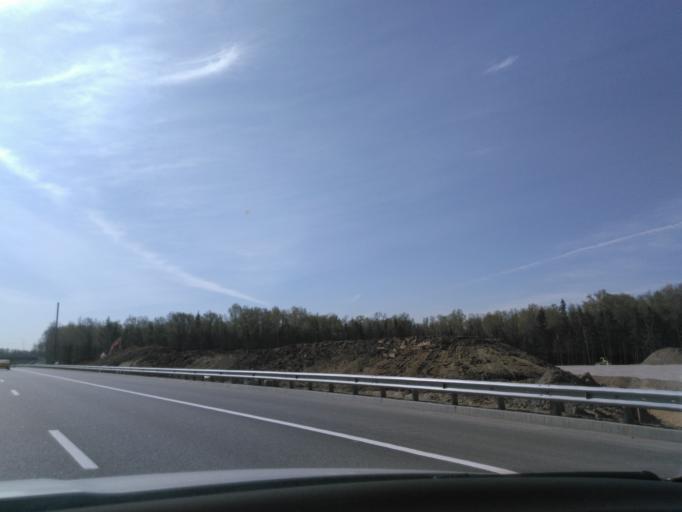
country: RU
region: Moscow
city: Khimki
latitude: 55.9480
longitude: 37.4396
